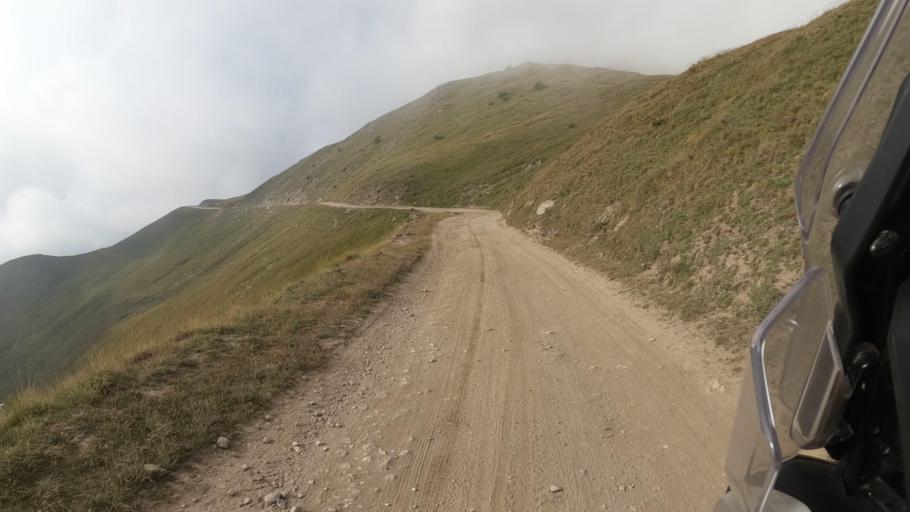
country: IT
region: Piedmont
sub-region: Provincia di Torino
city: Pragelato-Rua
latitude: 45.0469
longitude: 6.9329
